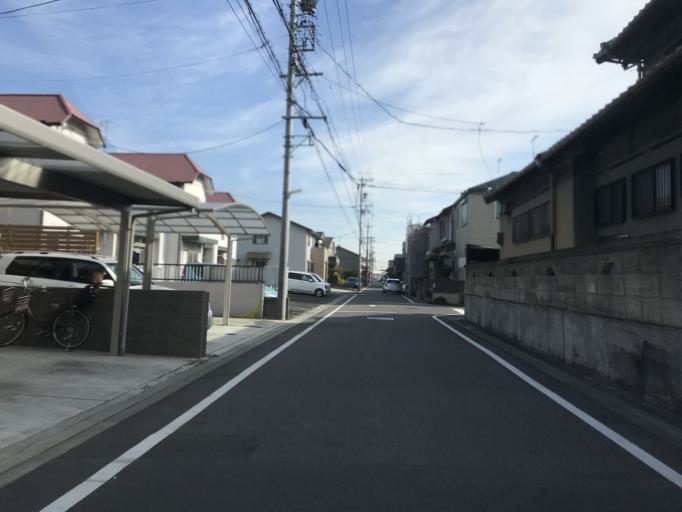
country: JP
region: Aichi
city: Inazawa
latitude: 35.2218
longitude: 136.8307
